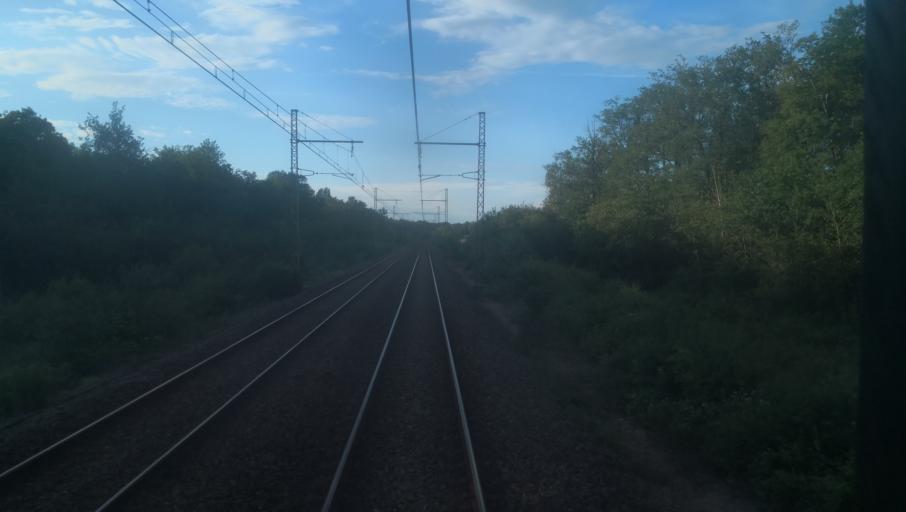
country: FR
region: Centre
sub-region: Departement de l'Indre
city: Luant
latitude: 46.7458
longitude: 1.5937
